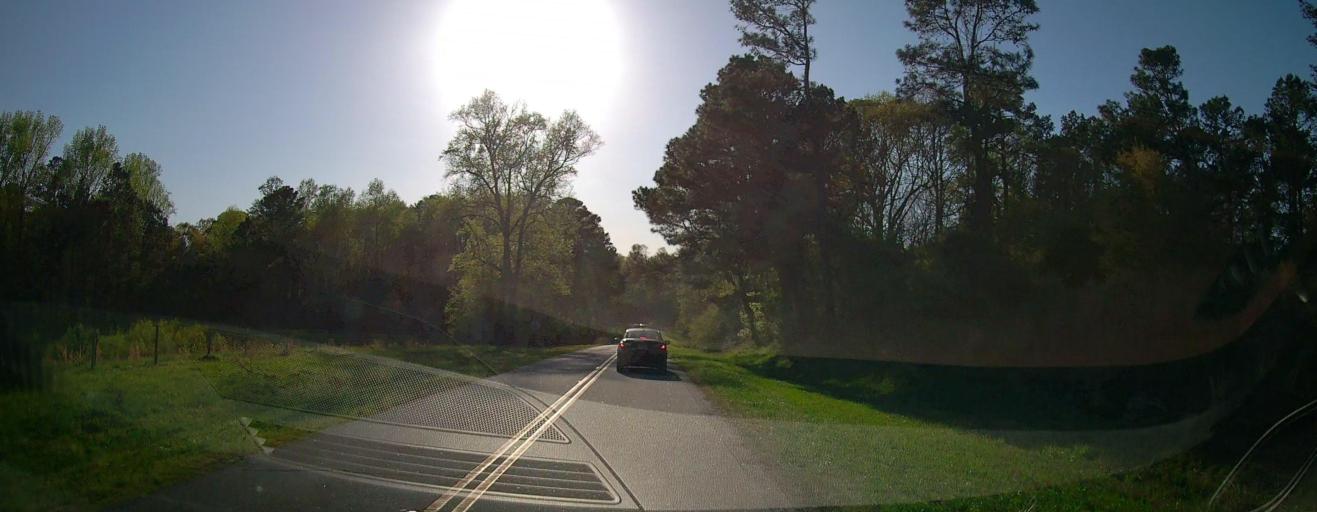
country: US
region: Georgia
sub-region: Butts County
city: Jackson
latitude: 33.3085
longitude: -83.9016
